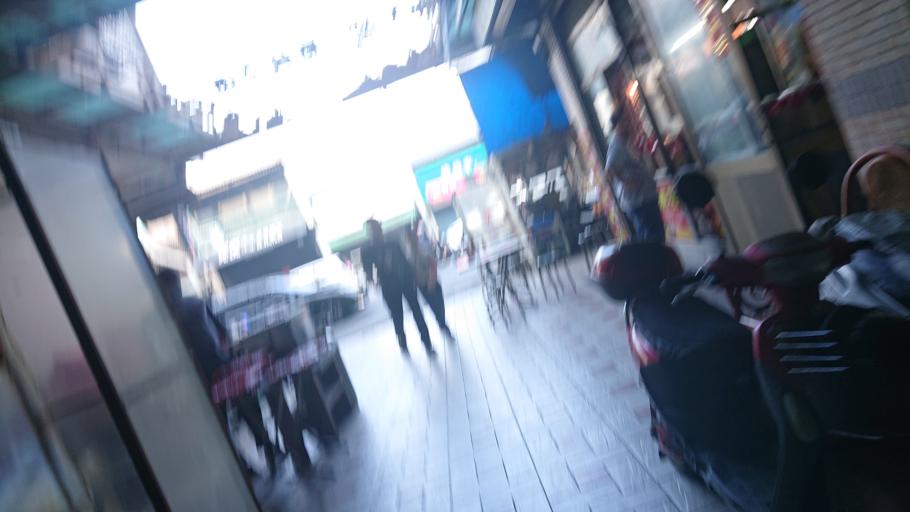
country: TW
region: Taiwan
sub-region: Chiayi
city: Taibao
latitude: 23.4666
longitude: 120.2442
